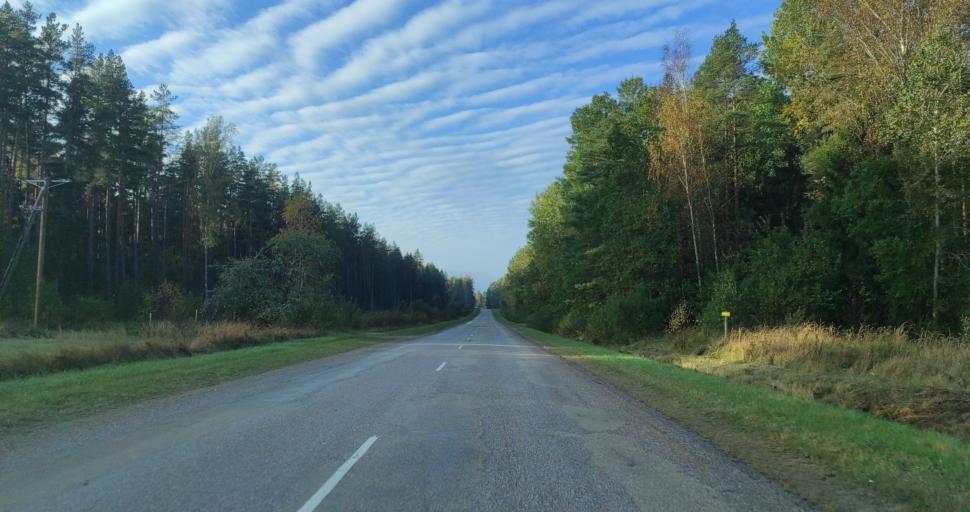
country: LV
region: Skrunda
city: Skrunda
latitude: 56.8002
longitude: 22.0058
